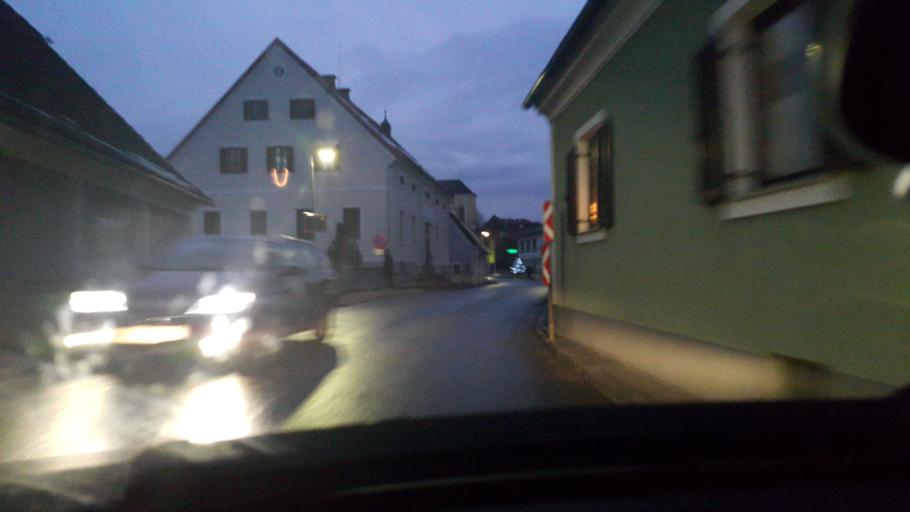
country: AT
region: Styria
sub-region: Politischer Bezirk Leibnitz
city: Leutschach
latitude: 46.6648
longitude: 15.4698
